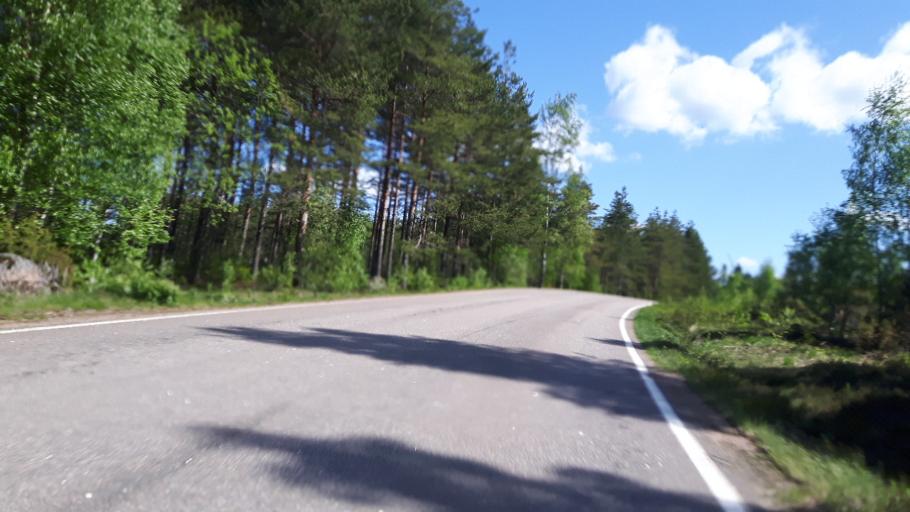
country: FI
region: Kymenlaakso
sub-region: Kotka-Hamina
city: Hamina
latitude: 60.5129
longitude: 27.4044
